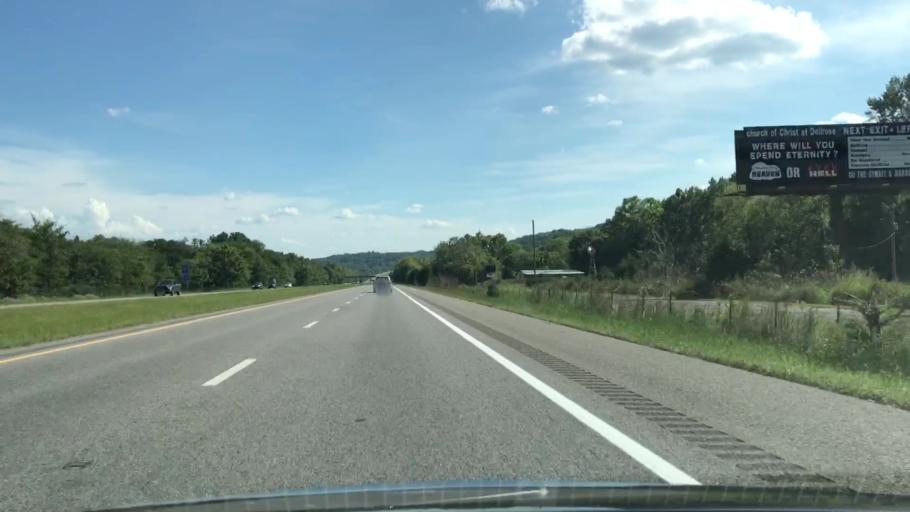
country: US
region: Alabama
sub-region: Limestone County
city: Ardmore
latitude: 35.1457
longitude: -86.8789
